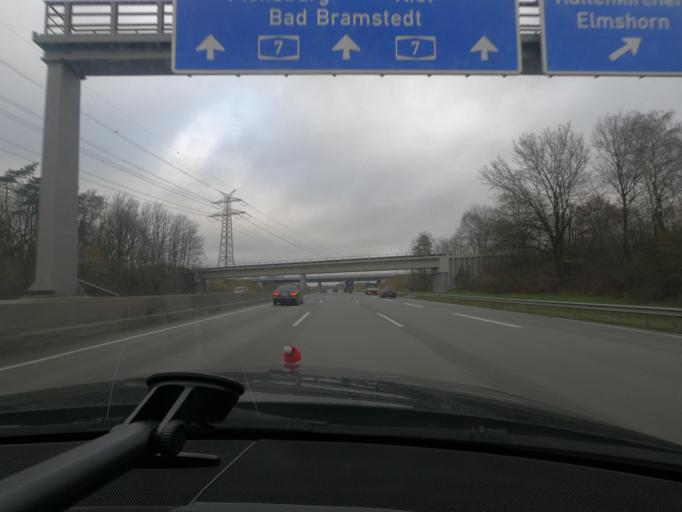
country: DE
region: Schleswig-Holstein
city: Nutzen
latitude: 53.8470
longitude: 9.9347
